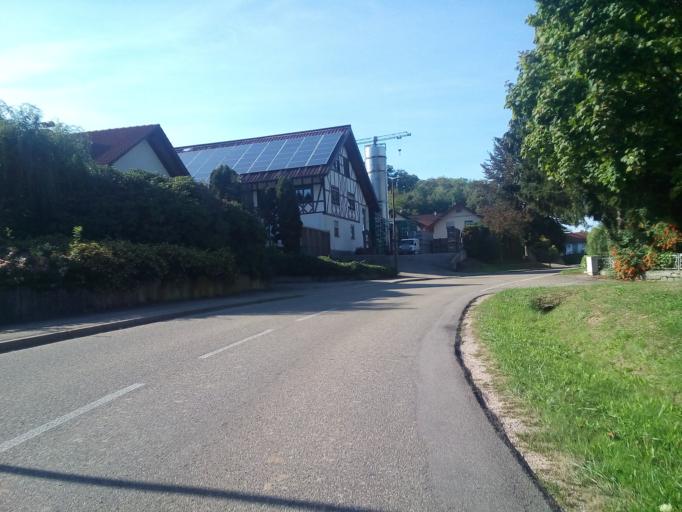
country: DE
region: Baden-Wuerttemberg
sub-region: Freiburg Region
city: Sasbach
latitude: 48.6309
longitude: 8.1051
